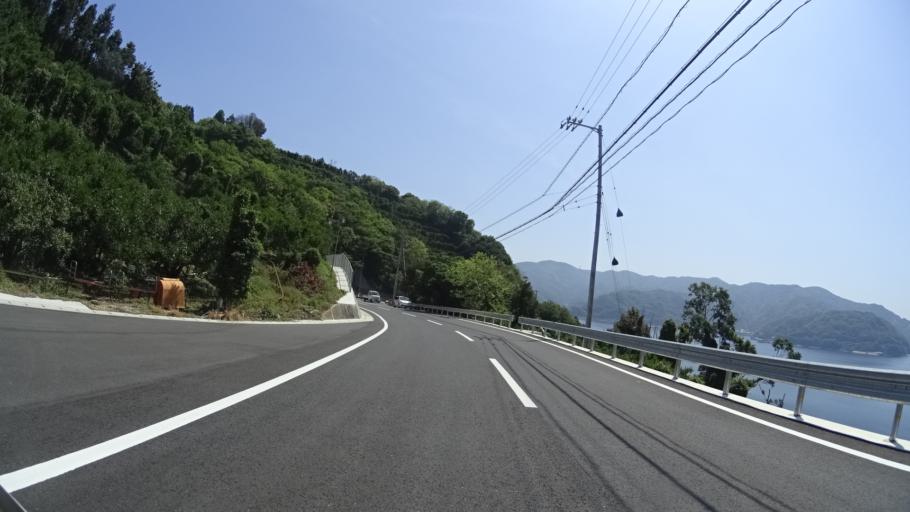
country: JP
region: Ehime
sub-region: Nishiuwa-gun
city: Ikata-cho
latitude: 33.3894
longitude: 132.1025
